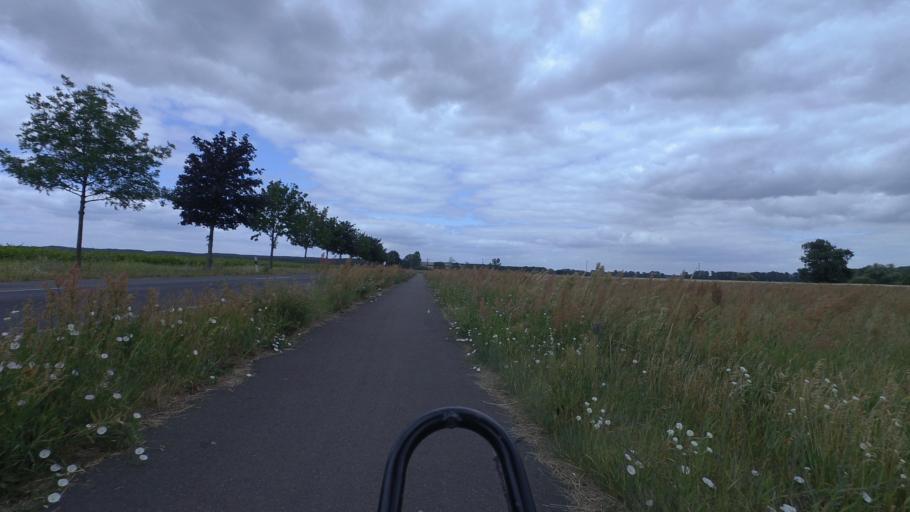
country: DE
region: Brandenburg
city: Trebbin
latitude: 52.2227
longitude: 13.1989
